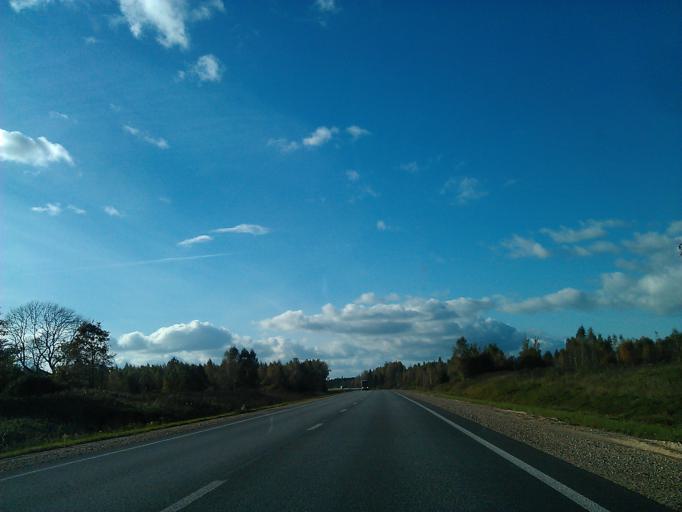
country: LV
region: Koknese
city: Koknese
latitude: 56.6943
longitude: 25.3493
